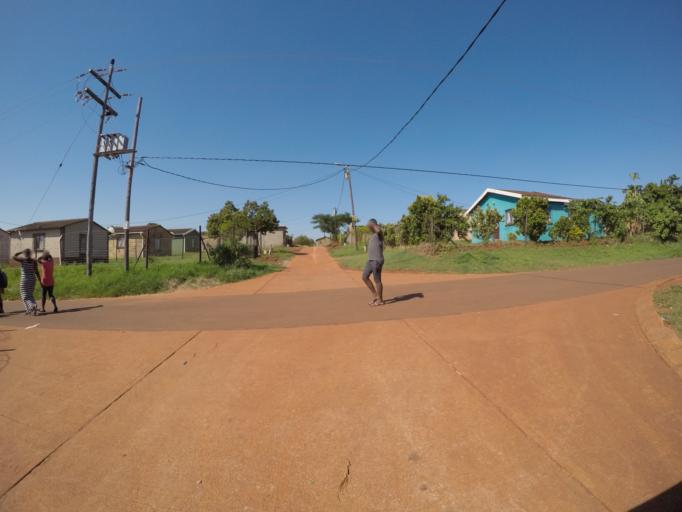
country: ZA
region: KwaZulu-Natal
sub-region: uThungulu District Municipality
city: Empangeni
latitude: -28.7732
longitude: 31.8788
